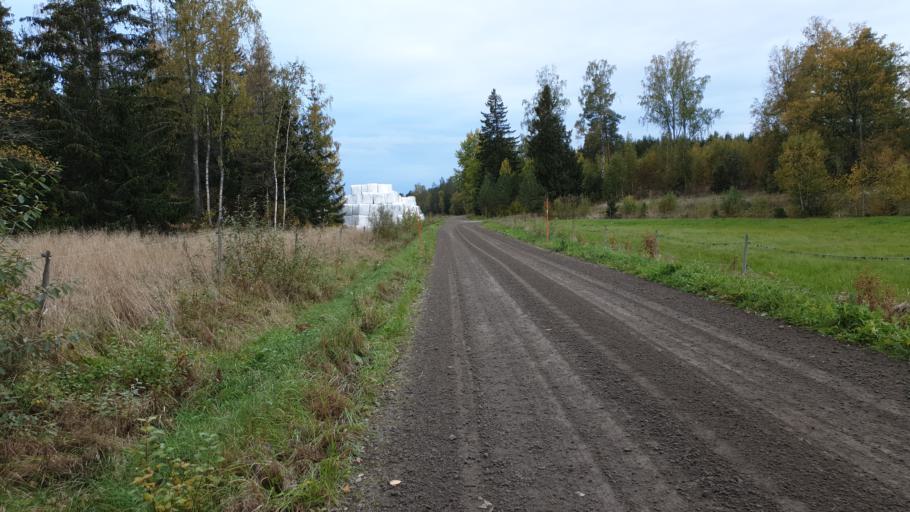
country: SE
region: Vaestmanland
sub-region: Sala Kommun
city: Sala
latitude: 59.8180
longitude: 16.6546
